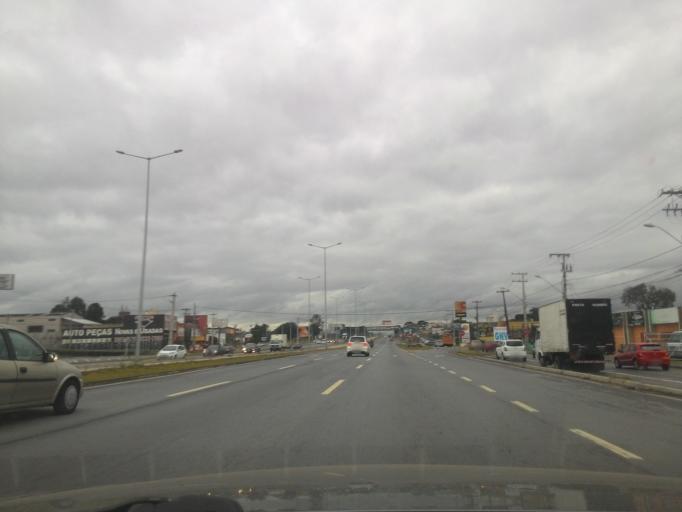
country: BR
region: Parana
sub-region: Sao Jose Dos Pinhais
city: Sao Jose dos Pinhais
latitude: -25.5249
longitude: -49.2964
